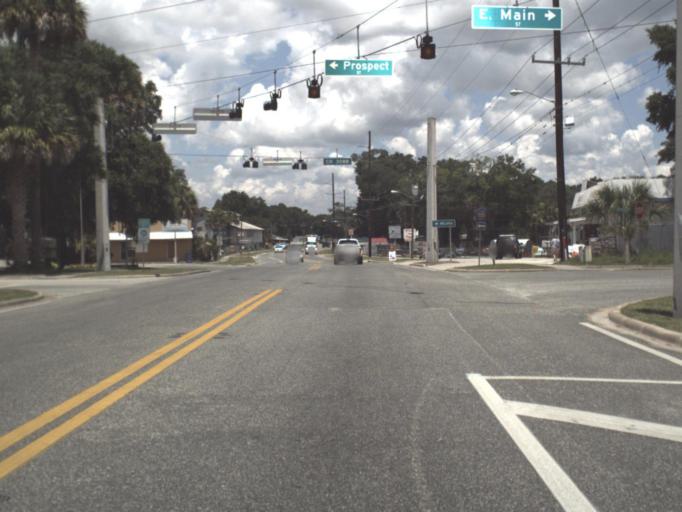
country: US
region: Florida
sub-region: Putnam County
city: Crescent City
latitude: 29.4962
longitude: -81.5939
